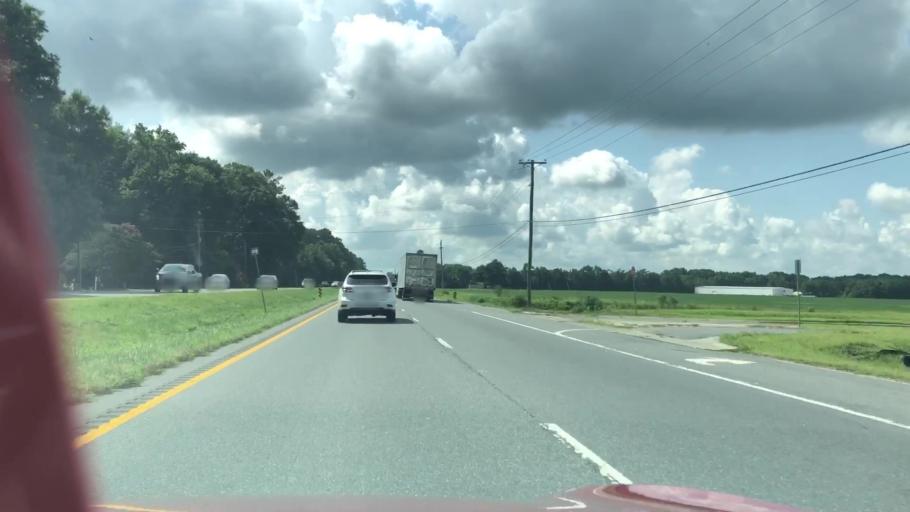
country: US
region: Virginia
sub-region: Accomack County
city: Wattsville
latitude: 37.9044
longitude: -75.5491
